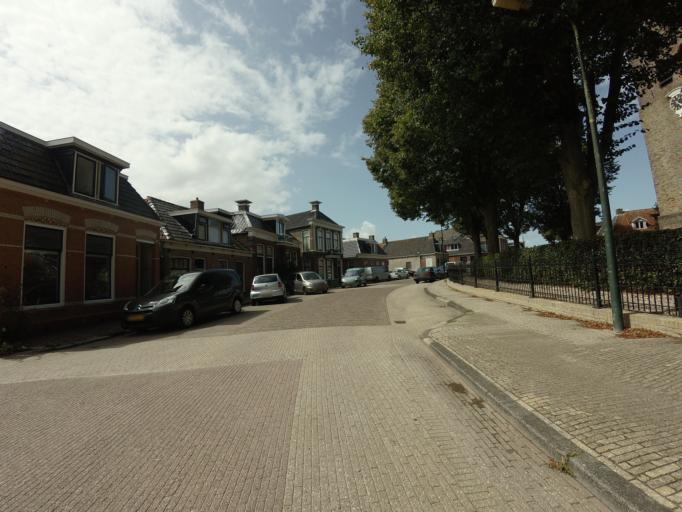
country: NL
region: Friesland
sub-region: Gemeente Harlingen
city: Harlingen
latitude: 53.1152
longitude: 5.4405
